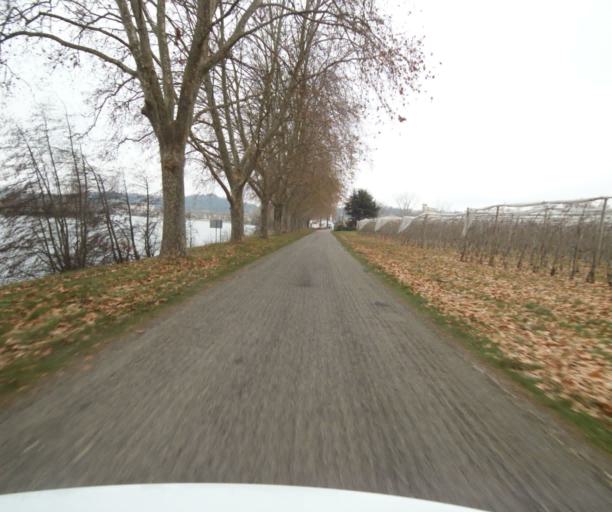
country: FR
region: Midi-Pyrenees
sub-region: Departement du Tarn-et-Garonne
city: Moissac
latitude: 44.0959
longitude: 1.0942
